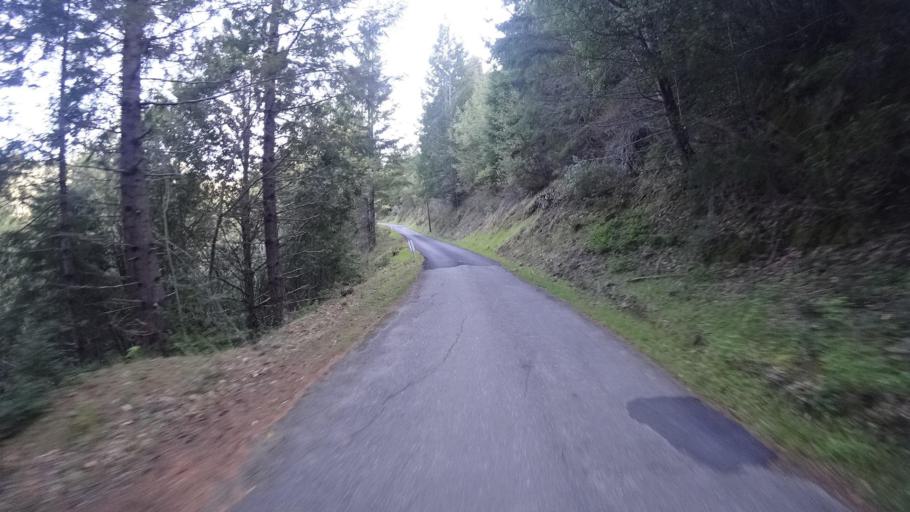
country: US
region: California
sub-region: Humboldt County
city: Blue Lake
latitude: 40.7059
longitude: -123.9365
